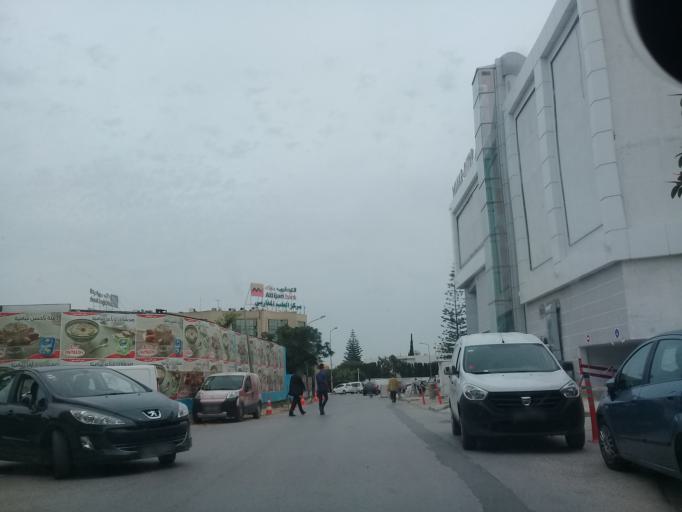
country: TN
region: Tunis
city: Tunis
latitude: 36.8430
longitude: 10.1631
